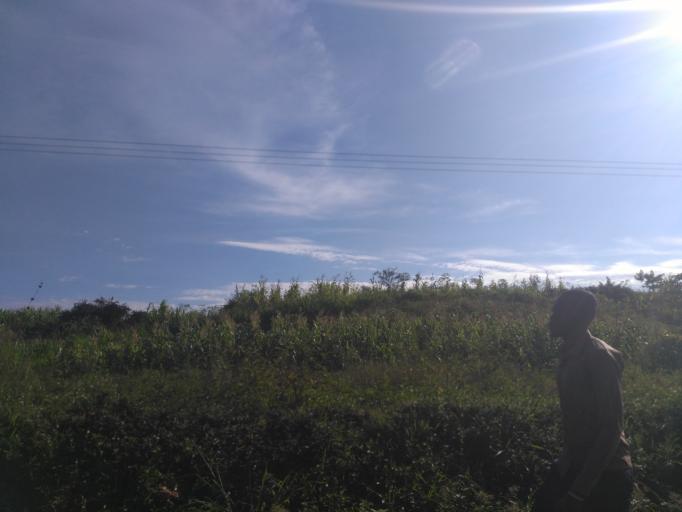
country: UG
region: Eastern Region
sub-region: Jinja District
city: Jinja
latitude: 0.4481
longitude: 33.1965
